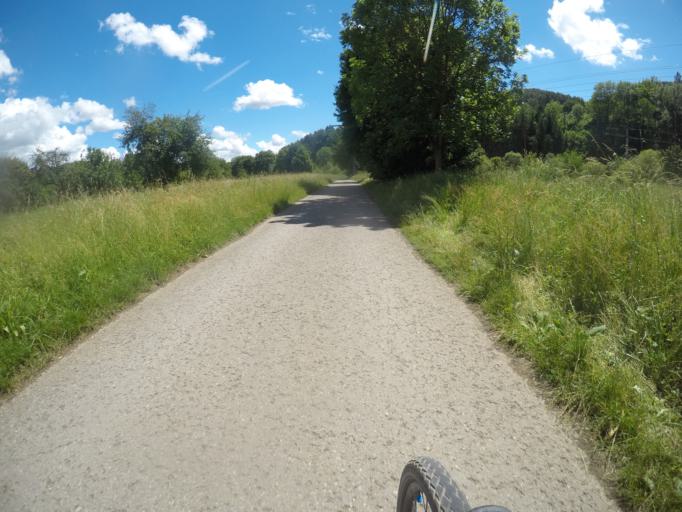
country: DE
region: Baden-Wuerttemberg
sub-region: Tuebingen Region
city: Haigerloch
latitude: 48.4442
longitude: 8.8033
